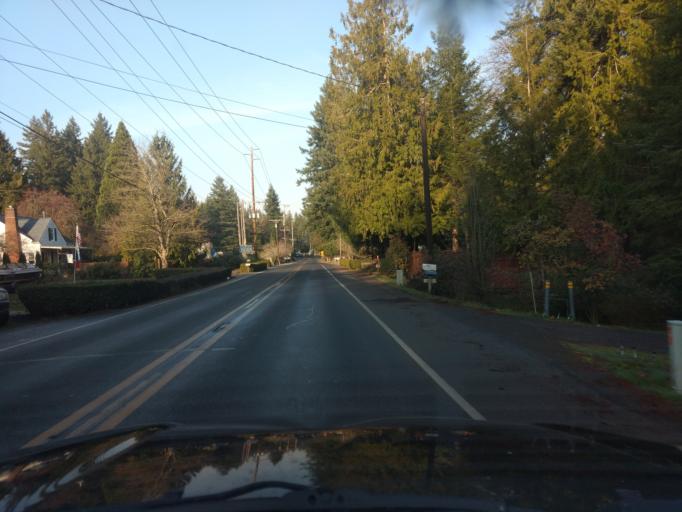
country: US
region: Washington
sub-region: Kitsap County
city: Erlands Point-Kitsap Lake
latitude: 47.5868
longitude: -122.7140
